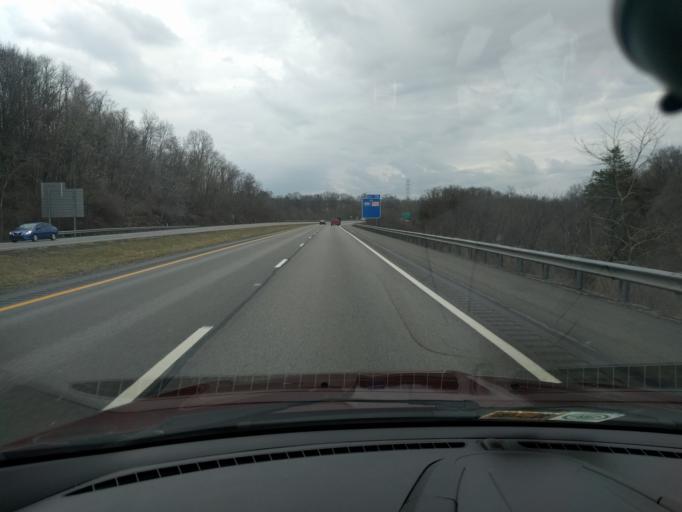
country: US
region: West Virginia
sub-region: Wood County
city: Boaz
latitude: 39.3007
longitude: -81.4901
